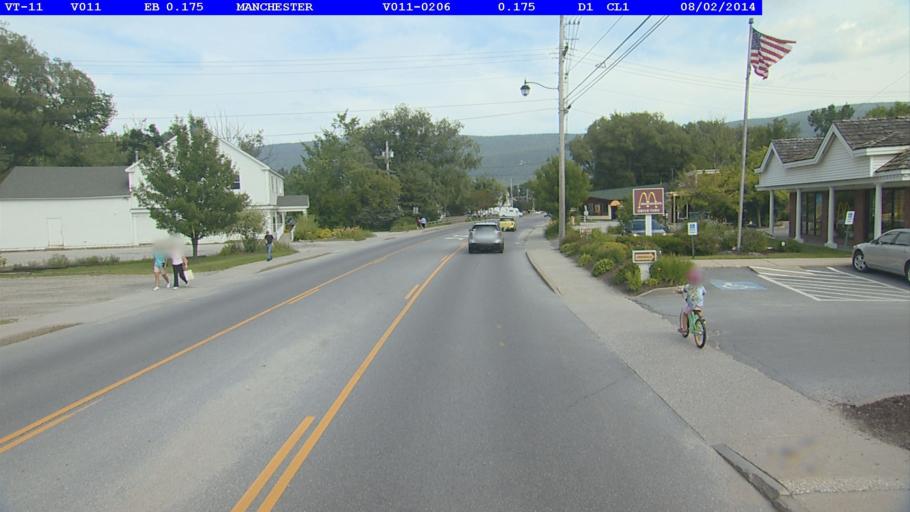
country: US
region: Vermont
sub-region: Bennington County
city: Manchester Center
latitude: 43.1752
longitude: -73.0543
